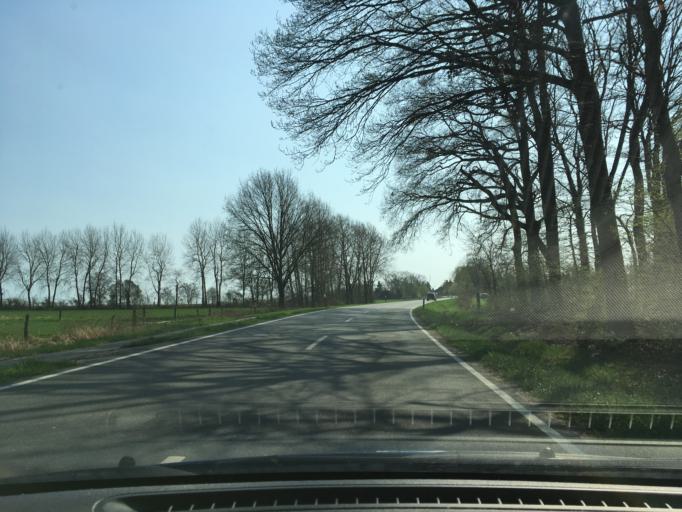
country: DE
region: Lower Saxony
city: Sudergellersen
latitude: 53.2203
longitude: 10.2976
